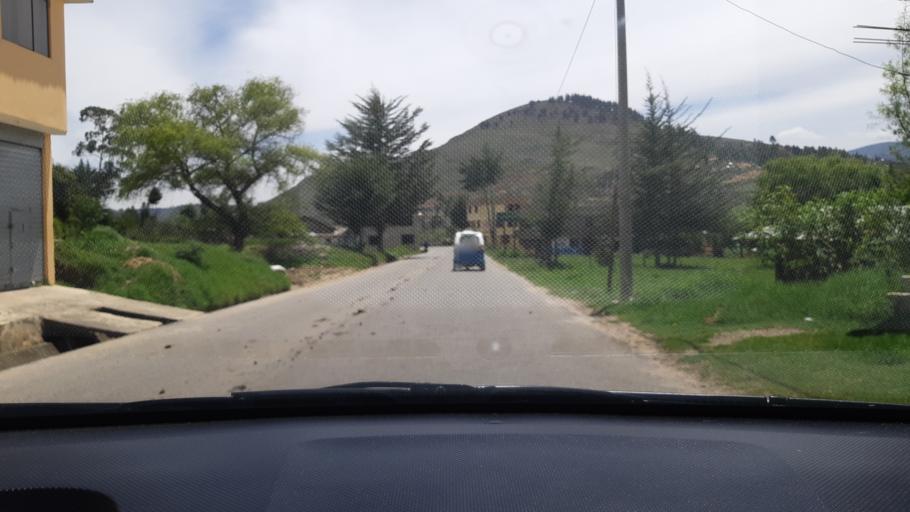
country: PE
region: Cajamarca
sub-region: Provincia de Cajamarca
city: Llacanora
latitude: -7.1808
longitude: -78.4545
